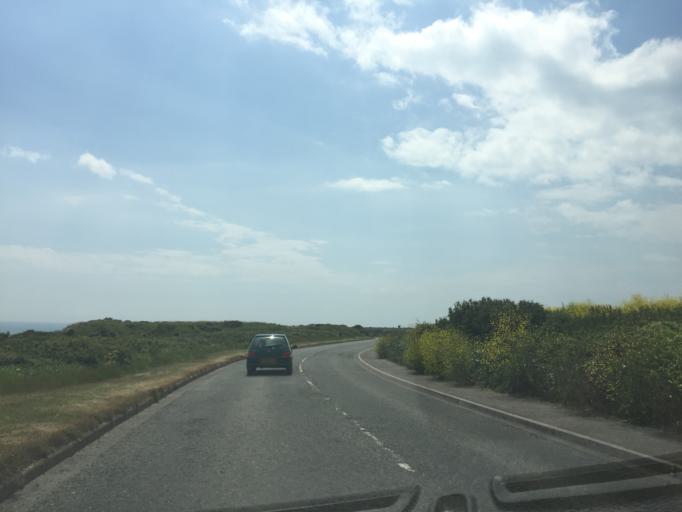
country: GB
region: England
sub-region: Dorset
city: Easton
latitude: 50.5347
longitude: -2.4330
